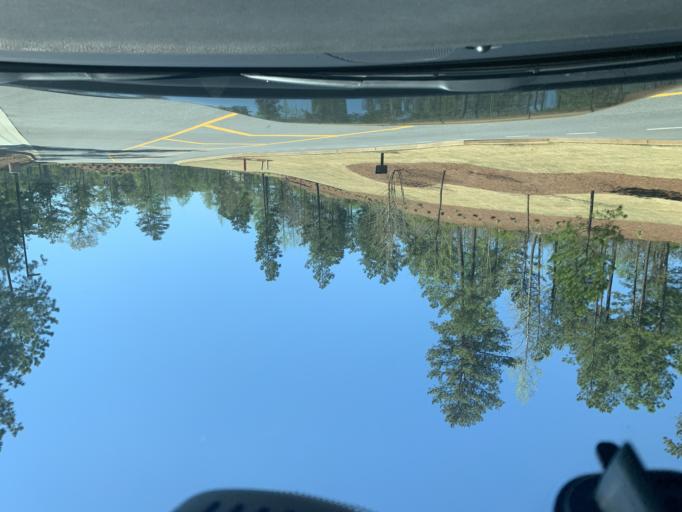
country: US
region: Georgia
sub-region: Fulton County
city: Milton
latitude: 34.1250
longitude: -84.2092
